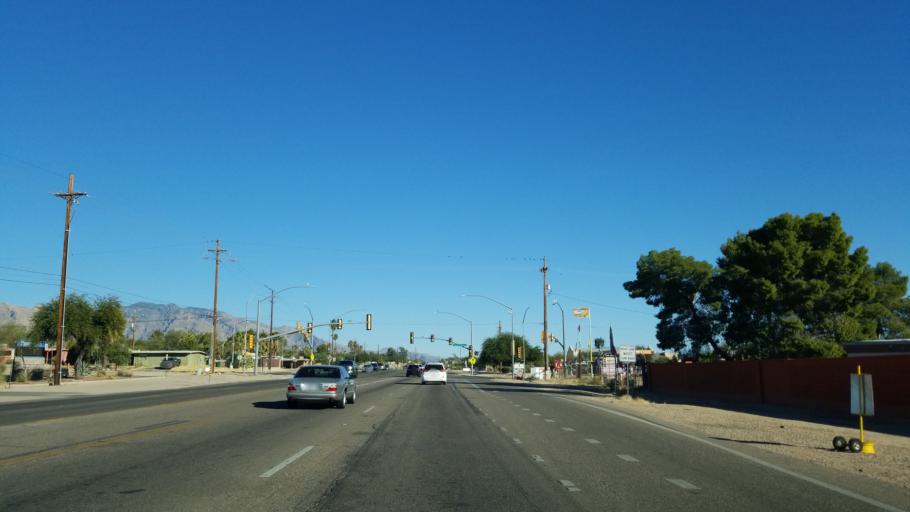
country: US
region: Arizona
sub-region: Pima County
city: Flowing Wells
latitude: 32.3232
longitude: -111.0388
